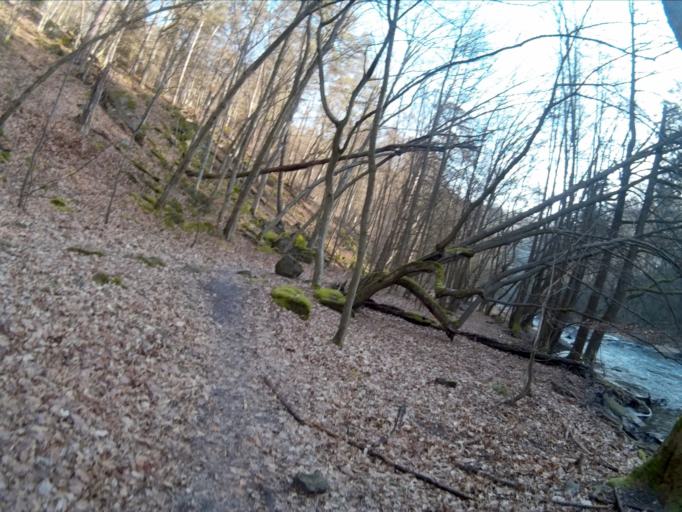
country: CZ
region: Vysocina
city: Namest' nad Oslavou
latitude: 49.1760
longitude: 16.1604
